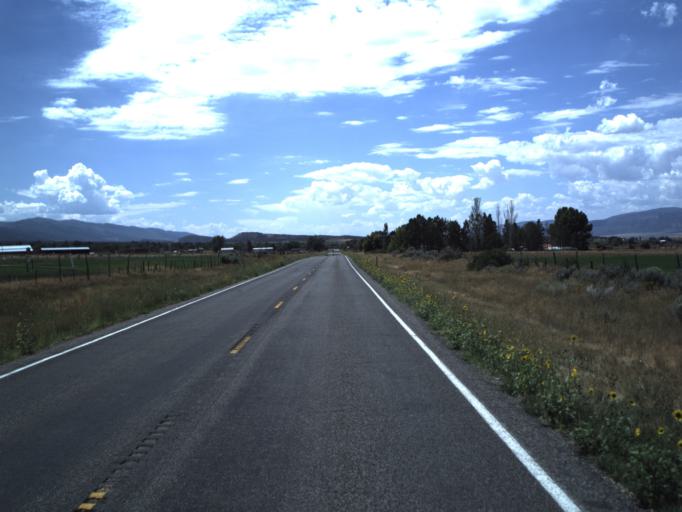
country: US
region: Utah
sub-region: Sanpete County
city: Mount Pleasant
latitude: 39.5048
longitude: -111.4855
